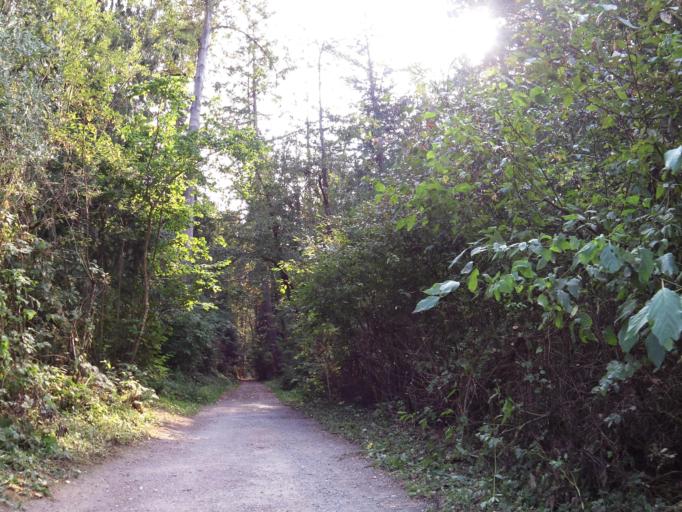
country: US
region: Washington
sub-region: Whatcom County
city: Bellingham
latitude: 48.7074
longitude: -122.4857
